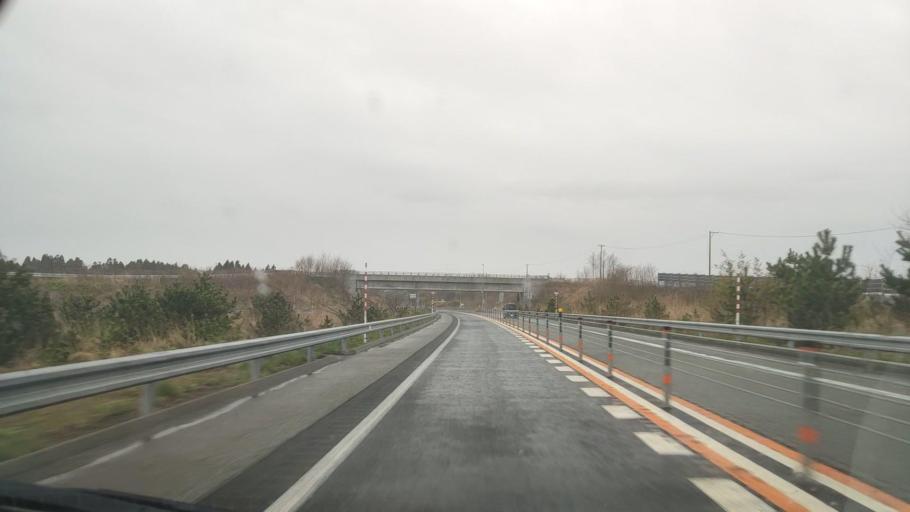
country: JP
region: Akita
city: Noshiromachi
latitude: 40.1534
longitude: 140.0225
